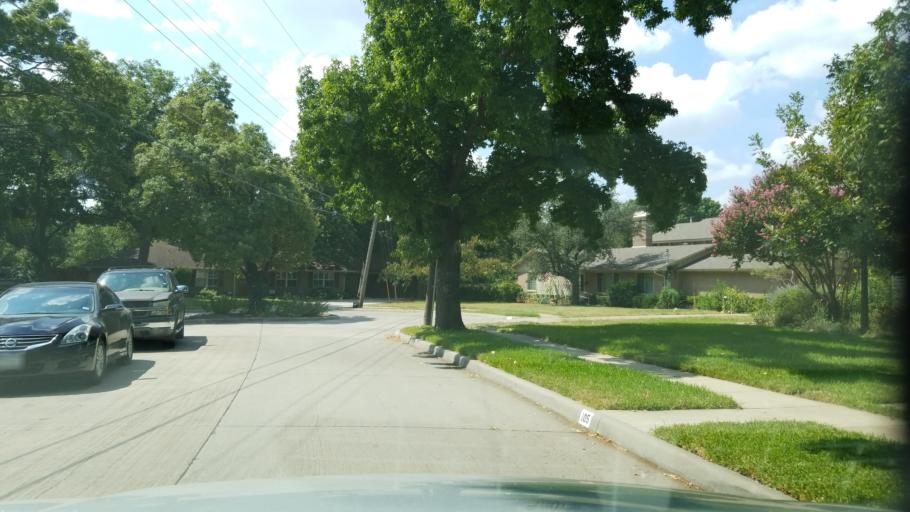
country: US
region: Texas
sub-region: Dallas County
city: Richardson
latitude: 32.9525
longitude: -96.7527
